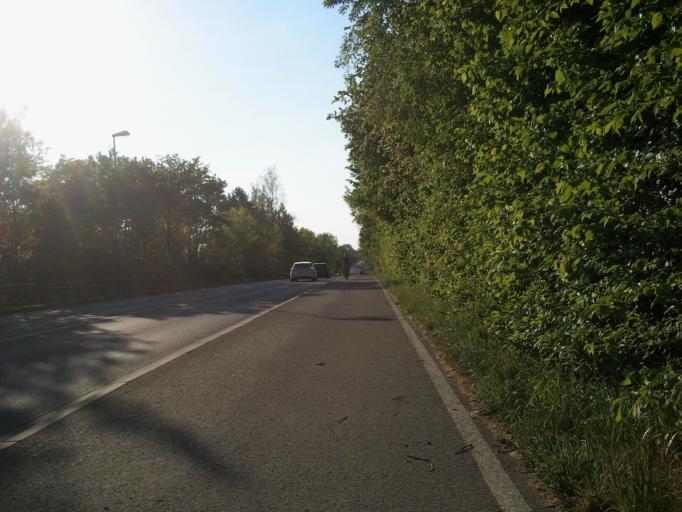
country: DE
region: Lower Saxony
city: Nienburg
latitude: 52.6218
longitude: 9.2380
